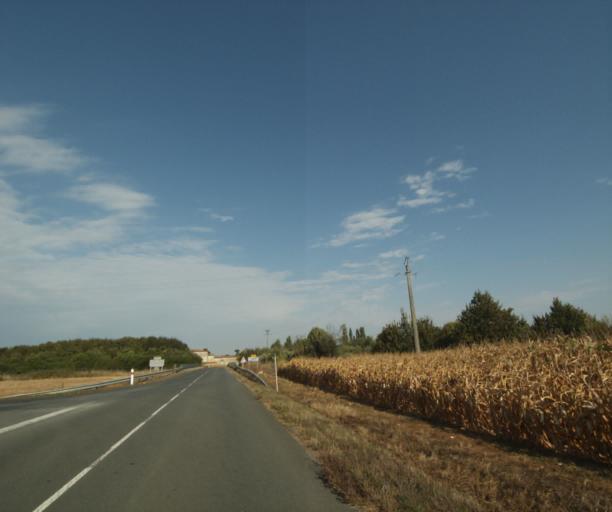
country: FR
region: Poitou-Charentes
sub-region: Departement de la Charente-Maritime
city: Tonnay-Charente
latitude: 45.9550
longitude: -0.8879
